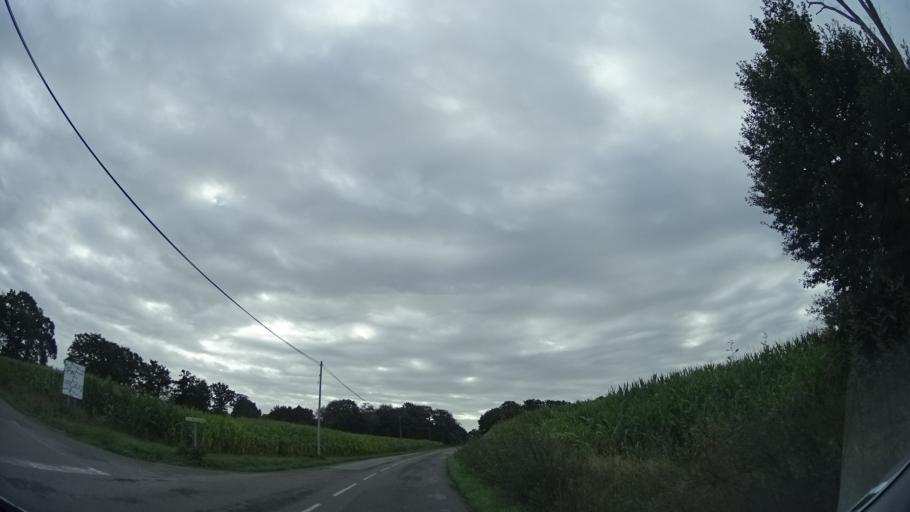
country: FR
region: Brittany
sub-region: Departement d'Ille-et-Vilaine
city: Dinge
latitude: 48.3554
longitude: -1.6975
